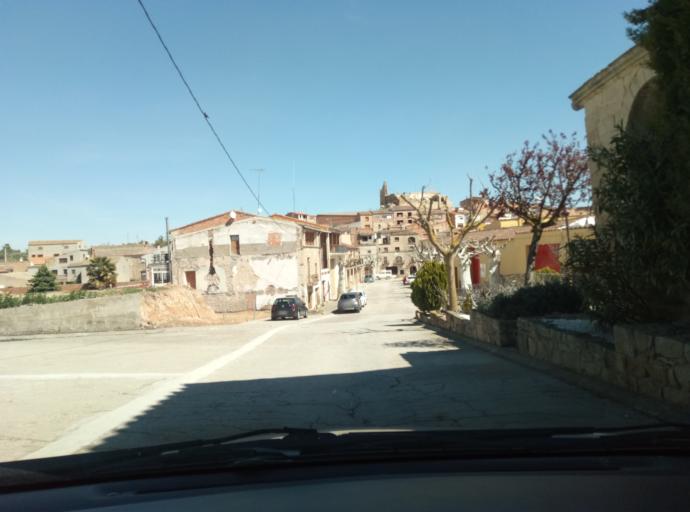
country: ES
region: Catalonia
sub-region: Provincia de Lleida
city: Vinaixa
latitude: 41.4219
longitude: 0.9344
